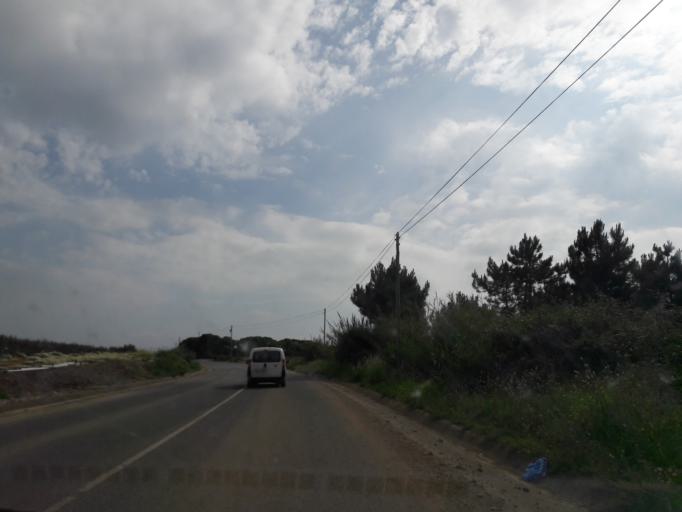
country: PT
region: Leiria
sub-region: Peniche
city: Atouguia da Baleia
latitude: 39.3527
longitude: -9.3219
